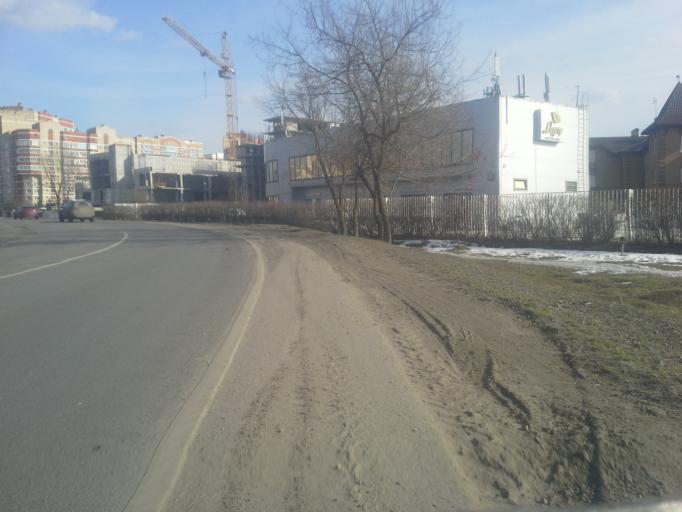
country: RU
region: Moskovskaya
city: Shcherbinka
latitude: 55.4727
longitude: 37.5388
